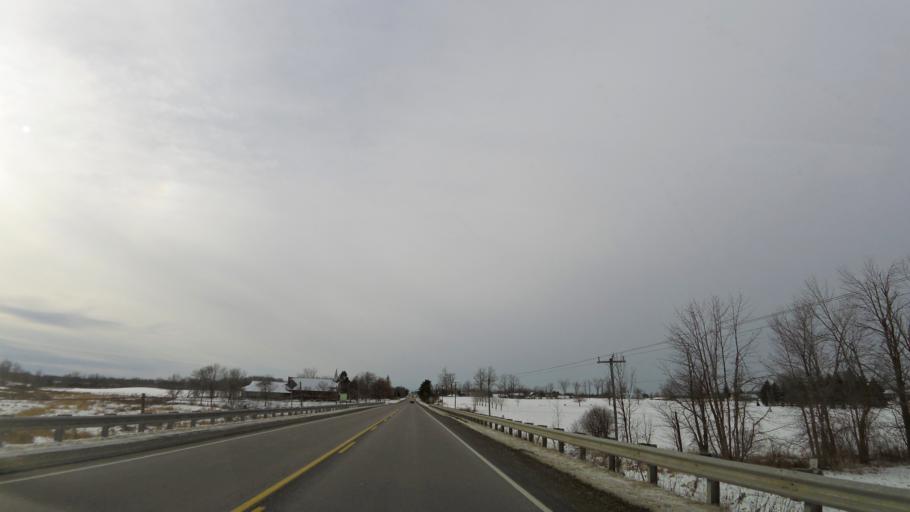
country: CA
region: Ontario
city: Ancaster
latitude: 43.2989
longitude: -79.9630
